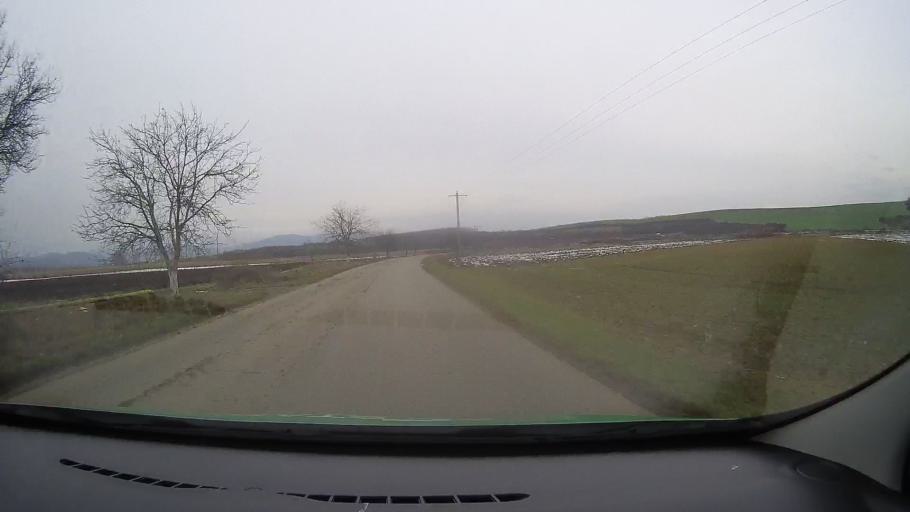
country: RO
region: Hunedoara
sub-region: Comuna Romos
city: Romos
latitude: 45.8602
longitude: 23.2720
